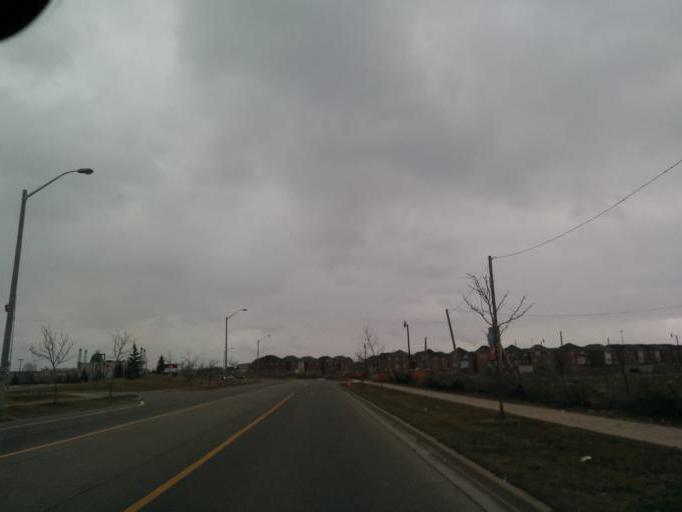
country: CA
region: Ontario
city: Brampton
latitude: 43.7398
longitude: -79.7725
